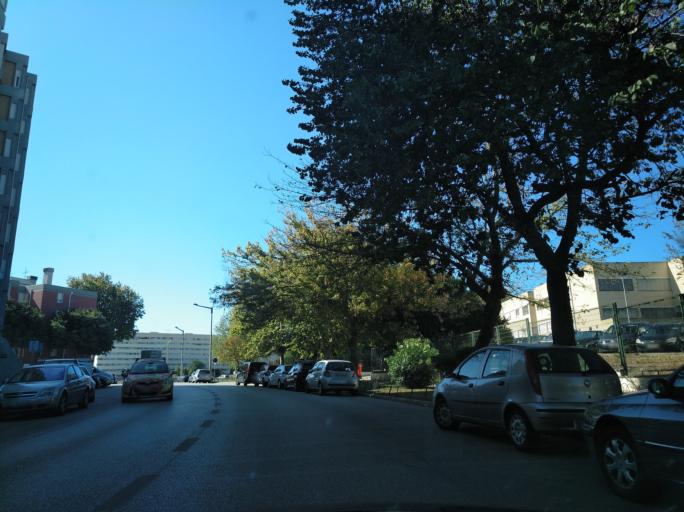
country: PT
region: Lisbon
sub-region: Loures
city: Moscavide
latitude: 38.7552
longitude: -9.1165
